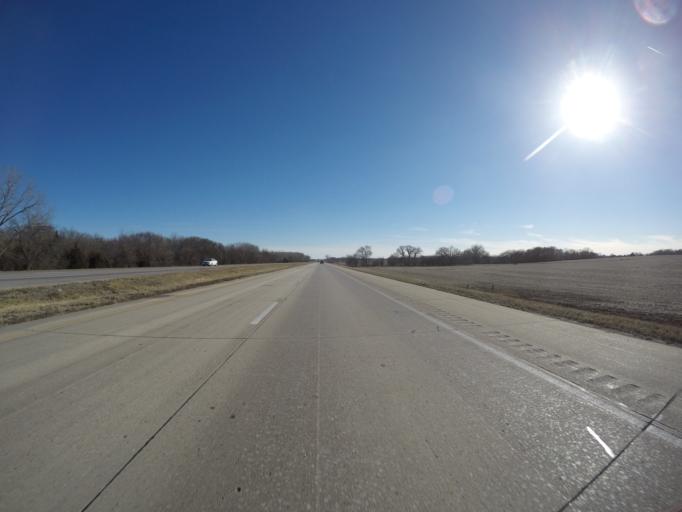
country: US
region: Nebraska
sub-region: Lancaster County
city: Lincoln
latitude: 40.7262
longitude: -96.7118
